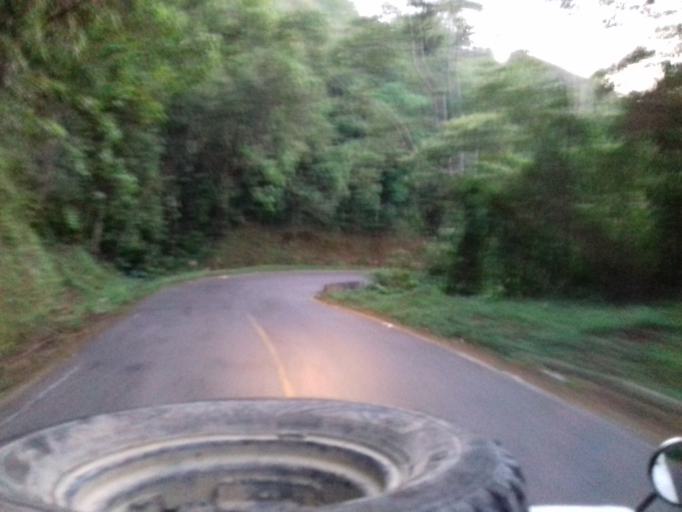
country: CO
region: Quindio
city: Salento
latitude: 4.6554
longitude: -75.5942
